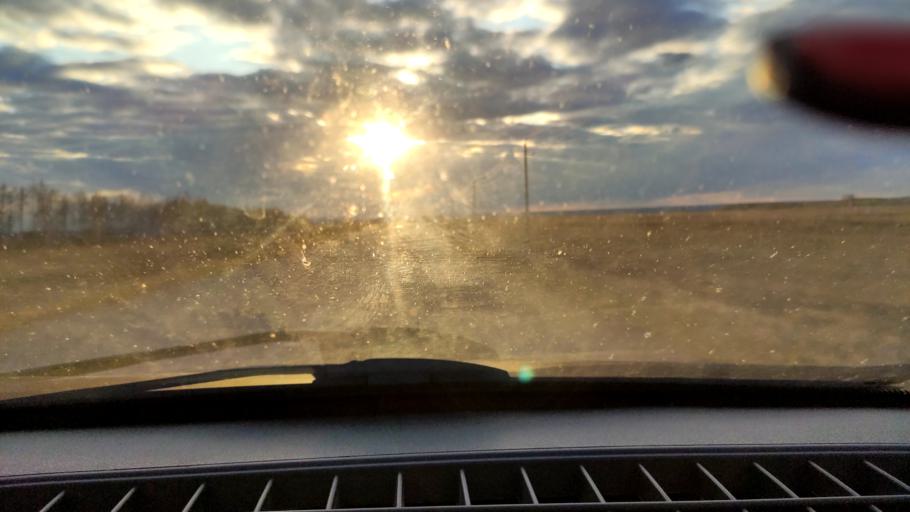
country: RU
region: Bashkortostan
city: Tolbazy
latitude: 54.0101
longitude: 55.5875
